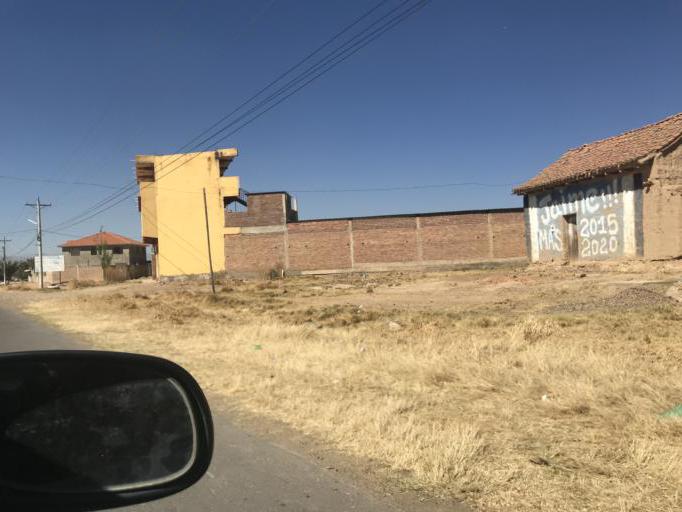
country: BO
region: Cochabamba
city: Cliza
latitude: -17.5985
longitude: -65.9595
